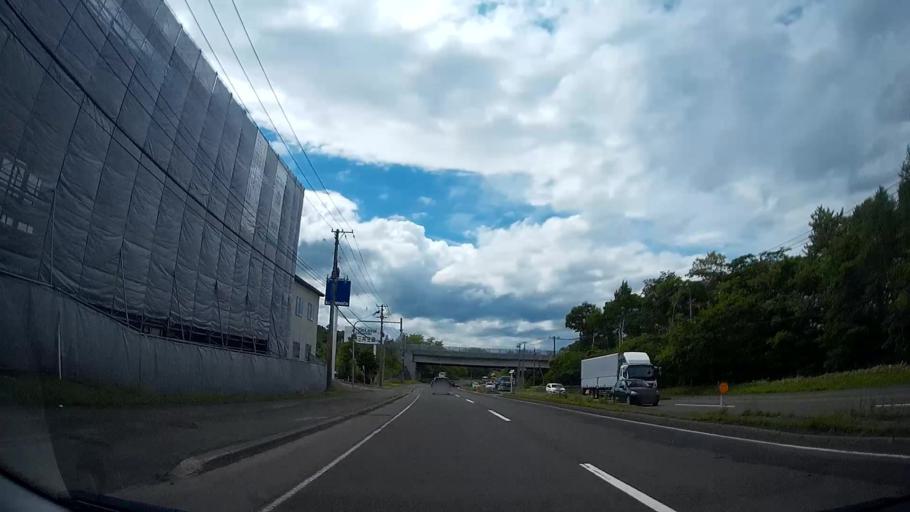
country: JP
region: Hokkaido
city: Chitose
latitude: 42.8572
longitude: 141.6068
